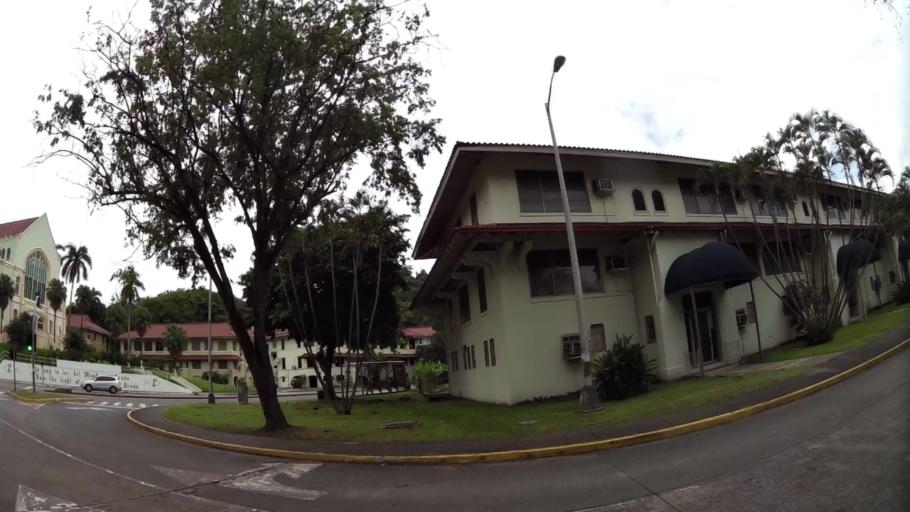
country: PA
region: Panama
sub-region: Distrito de Panama
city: Ancon
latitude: 8.9541
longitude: -79.5565
